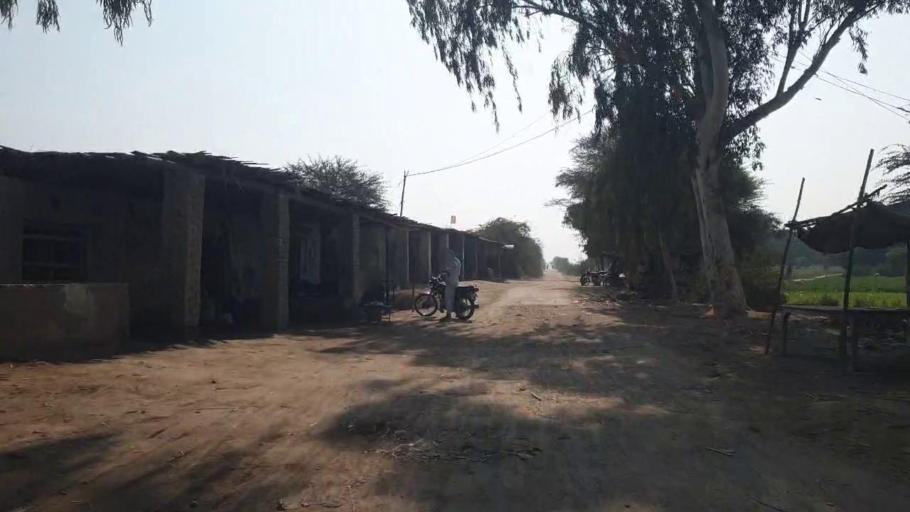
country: PK
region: Sindh
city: Tando Allahyar
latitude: 25.4825
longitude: 68.8017
